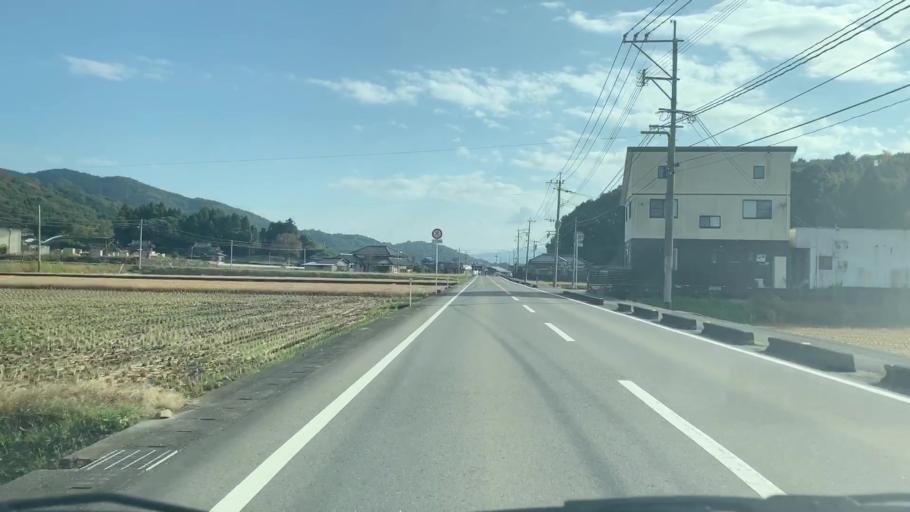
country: JP
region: Saga Prefecture
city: Kashima
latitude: 33.1540
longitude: 130.0641
